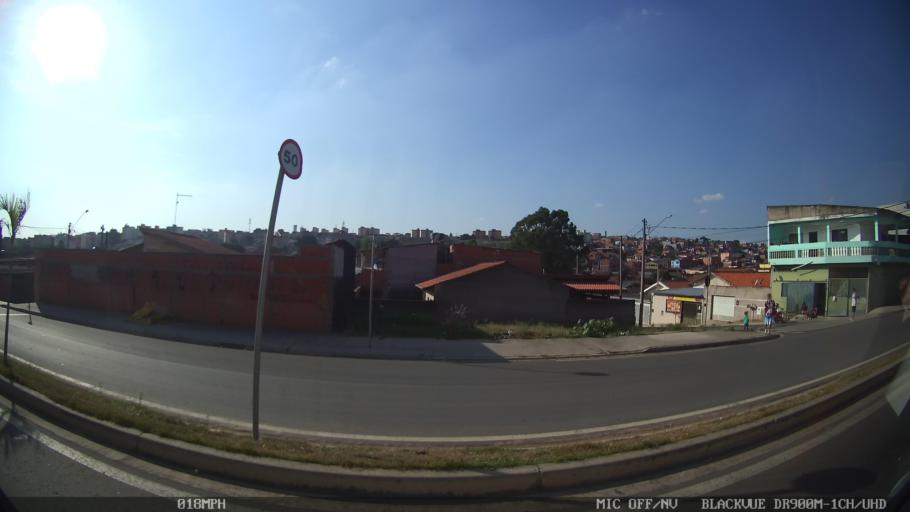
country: BR
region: Sao Paulo
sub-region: Campinas
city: Campinas
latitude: -22.9855
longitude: -47.1315
